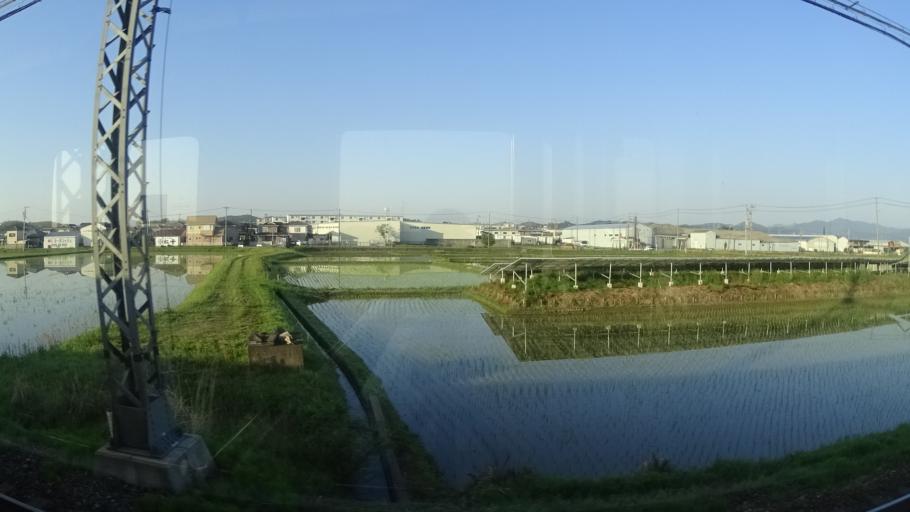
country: JP
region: Mie
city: Ise
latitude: 34.5548
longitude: 136.5692
